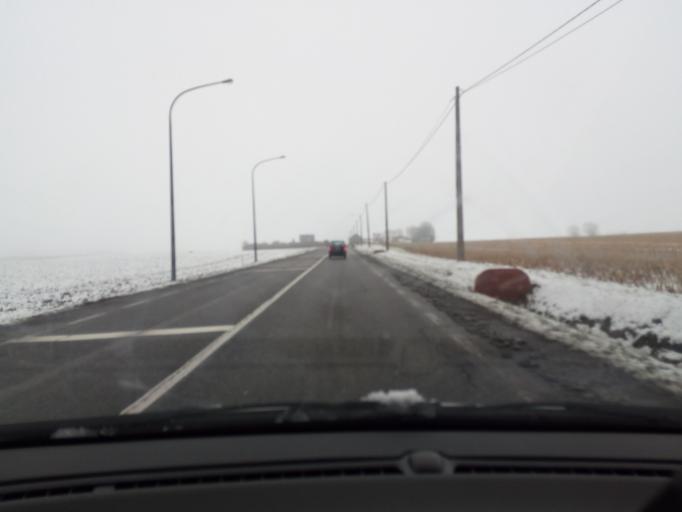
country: BE
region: Wallonia
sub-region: Province du Hainaut
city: Estinnes-au-Val
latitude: 50.4024
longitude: 4.1125
